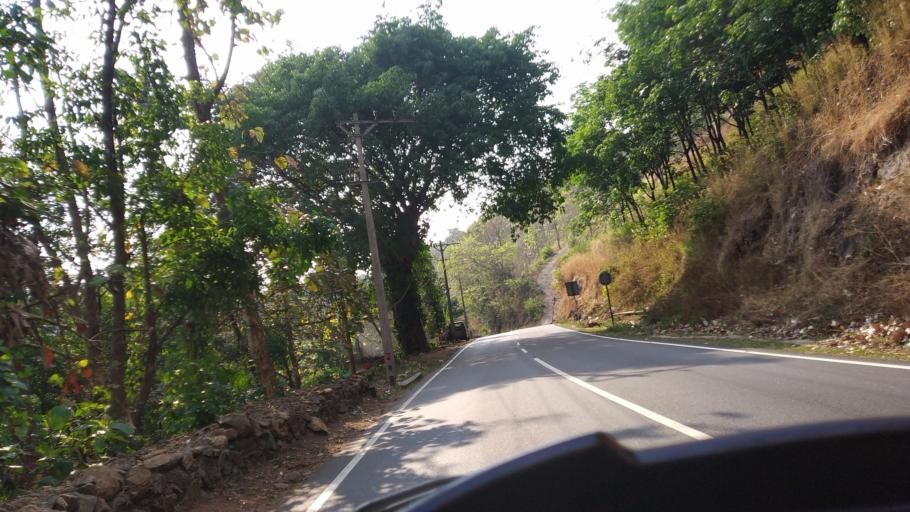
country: IN
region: Kerala
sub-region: Kottayam
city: Erattupetta
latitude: 9.5460
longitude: 76.9138
